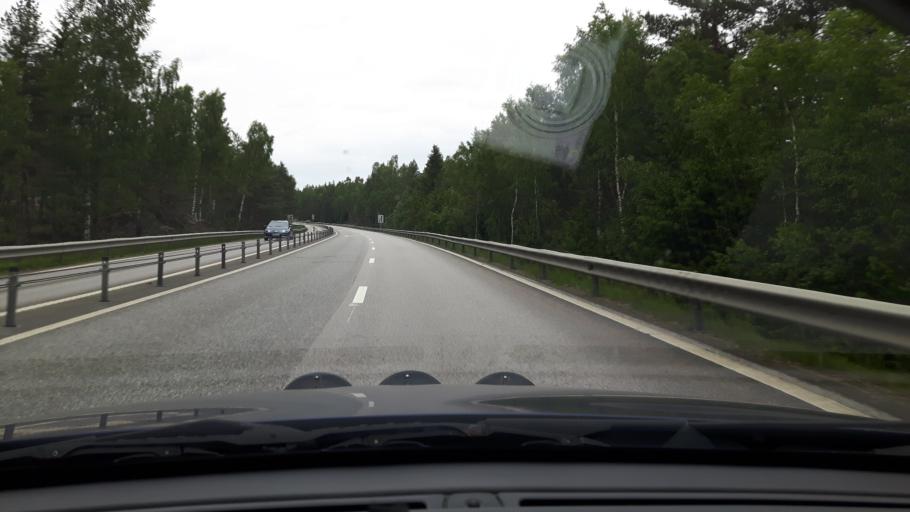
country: SE
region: OEstergoetland
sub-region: Norrkopings Kommun
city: Jursla
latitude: 58.7255
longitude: 16.1727
